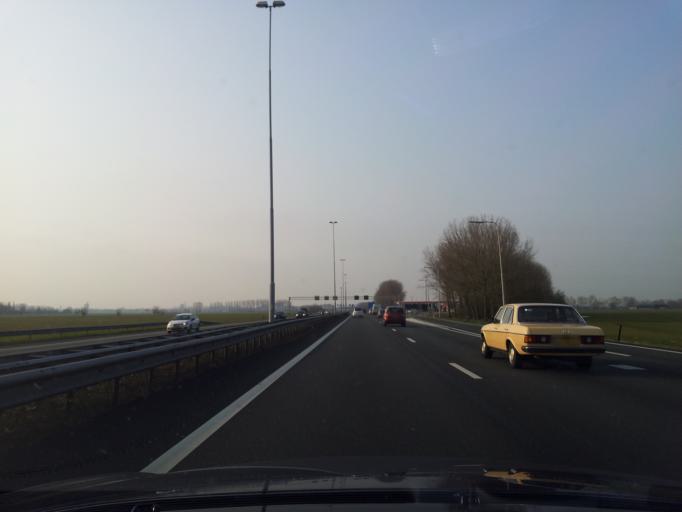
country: NL
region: South Holland
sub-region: Gemeente Gorinchem
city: Gorinchem
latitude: 51.8747
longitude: 4.9658
